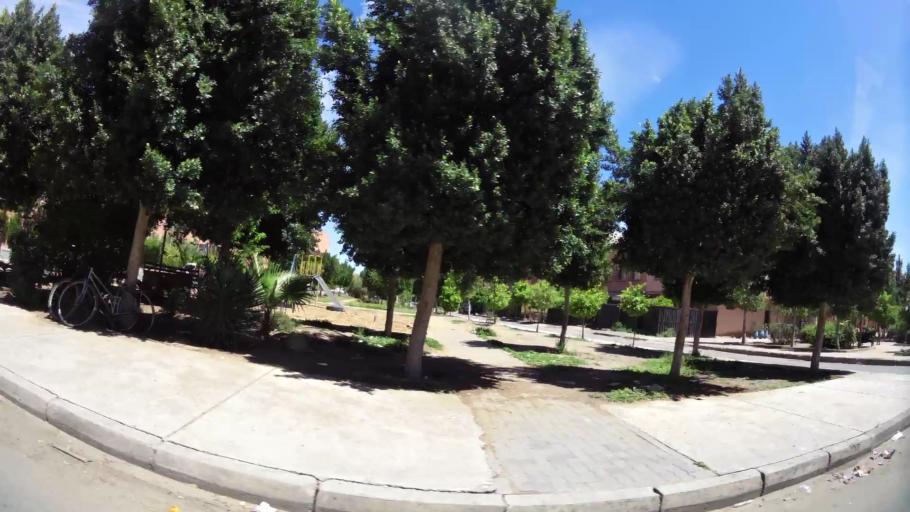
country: MA
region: Marrakech-Tensift-Al Haouz
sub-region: Marrakech
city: Marrakesh
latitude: 31.6391
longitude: -8.0461
